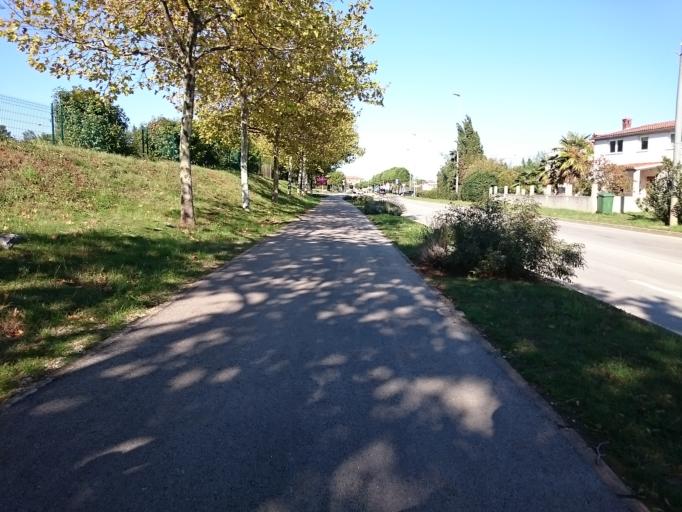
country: HR
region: Istarska
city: Umag
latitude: 45.4330
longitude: 13.5300
